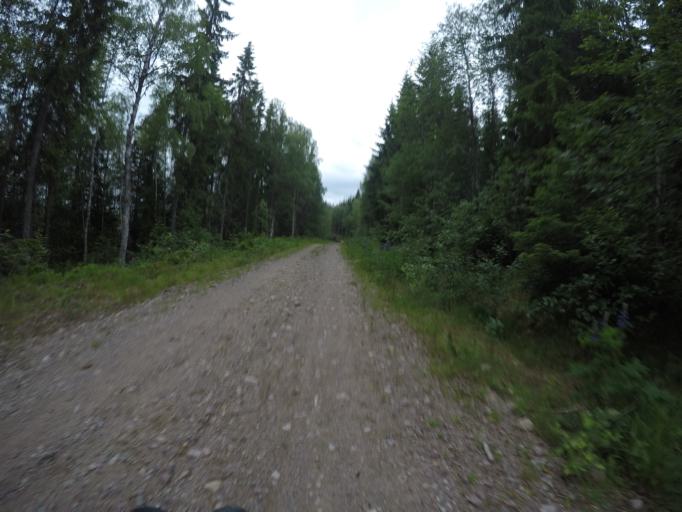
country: SE
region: Dalarna
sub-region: Ludvika Kommun
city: Abborrberget
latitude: 60.0380
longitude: 14.5955
